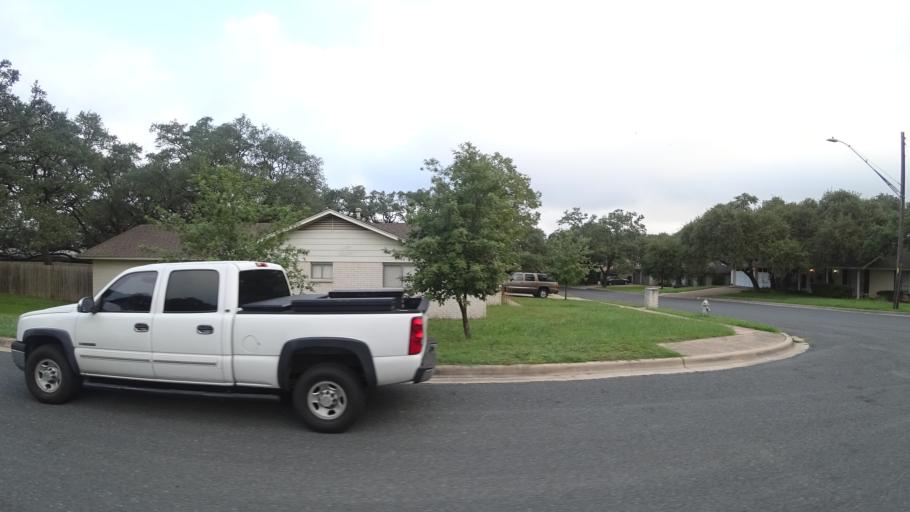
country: US
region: Texas
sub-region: Travis County
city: Austin
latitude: 30.3444
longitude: -97.6930
